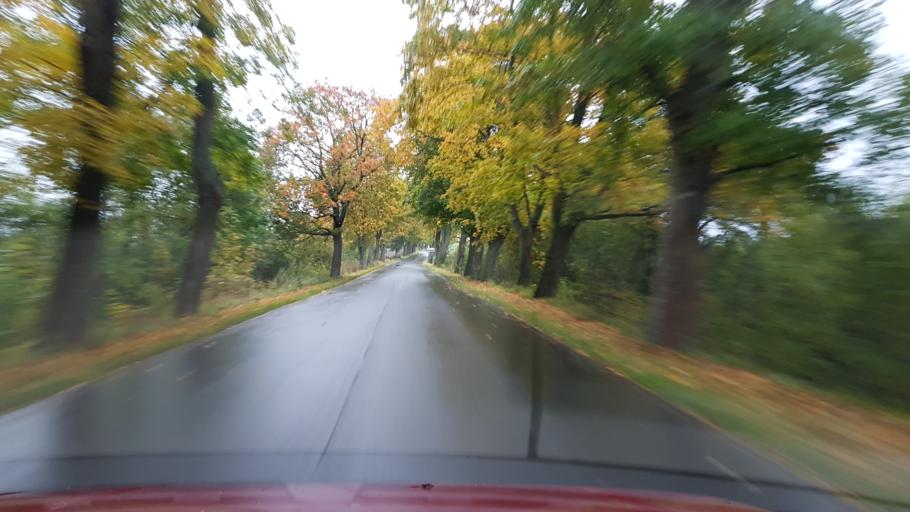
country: PL
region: West Pomeranian Voivodeship
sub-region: Koszalin
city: Koszalin
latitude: 54.1513
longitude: 16.1324
